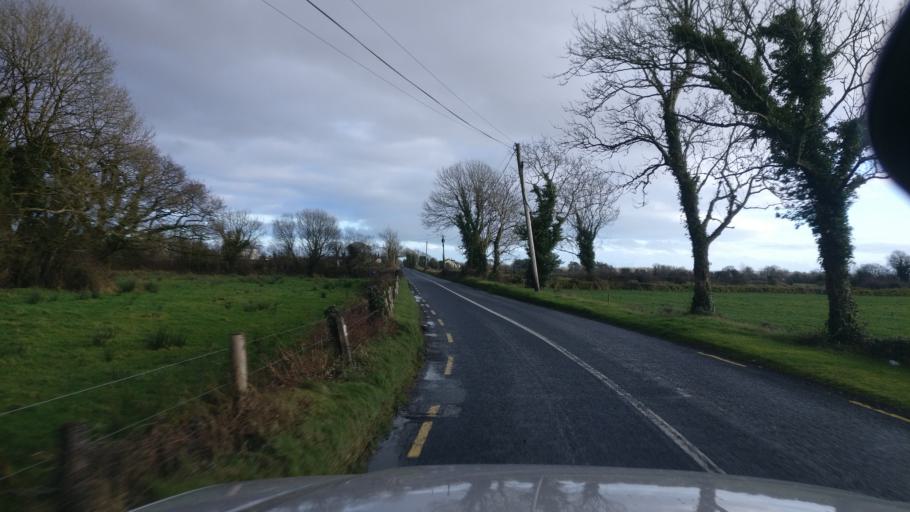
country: IE
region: Connaught
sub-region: County Galway
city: Athenry
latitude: 53.2930
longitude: -8.6462
